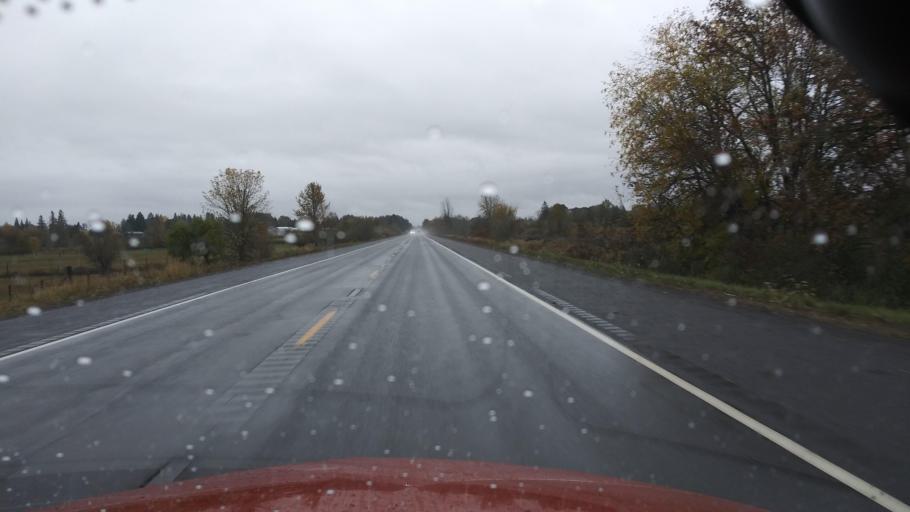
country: US
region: Oregon
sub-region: Washington County
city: Forest Grove
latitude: 45.4728
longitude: -123.1337
